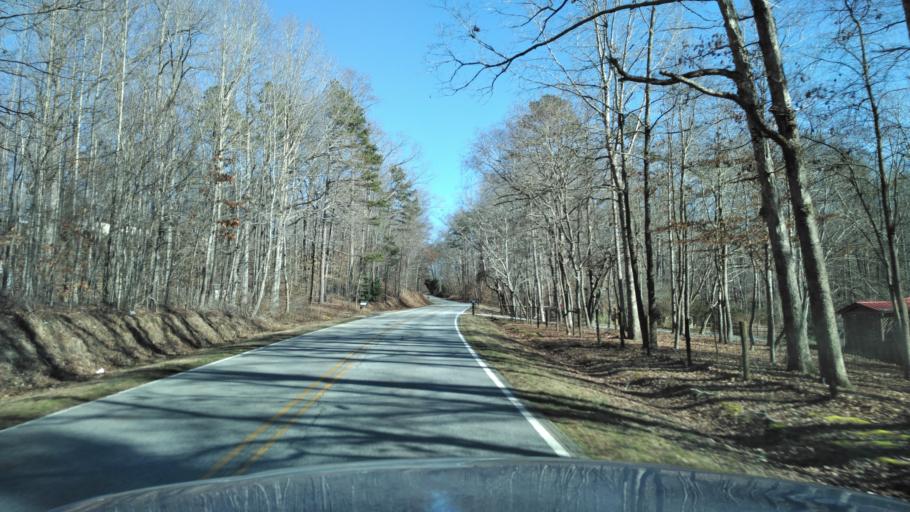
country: US
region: Georgia
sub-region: Hall County
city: Lula
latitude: 34.3180
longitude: -83.6844
